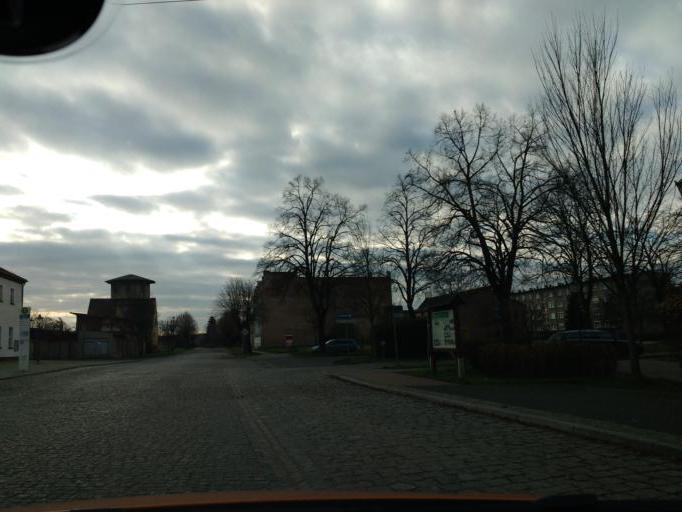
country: DE
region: Brandenburg
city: Wriezen
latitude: 52.7162
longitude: 14.1400
